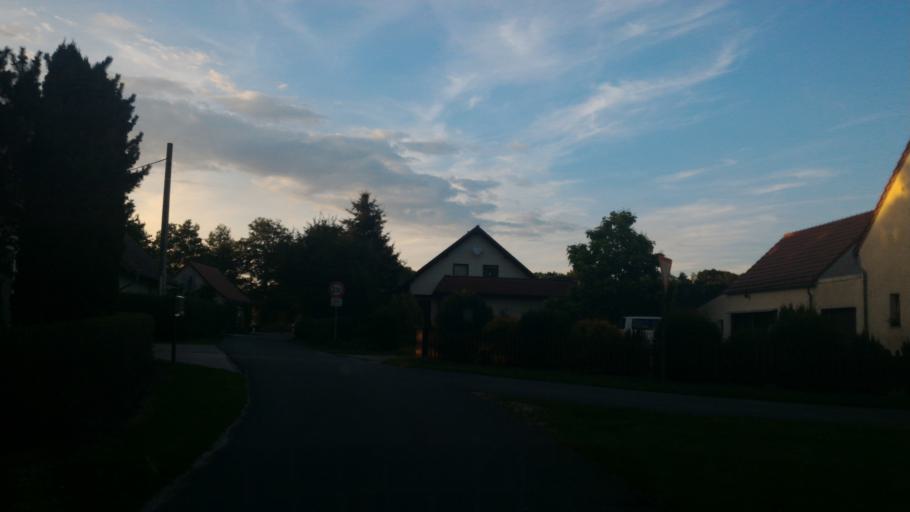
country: DE
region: Saxony
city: Horka
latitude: 51.2676
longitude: 14.9009
